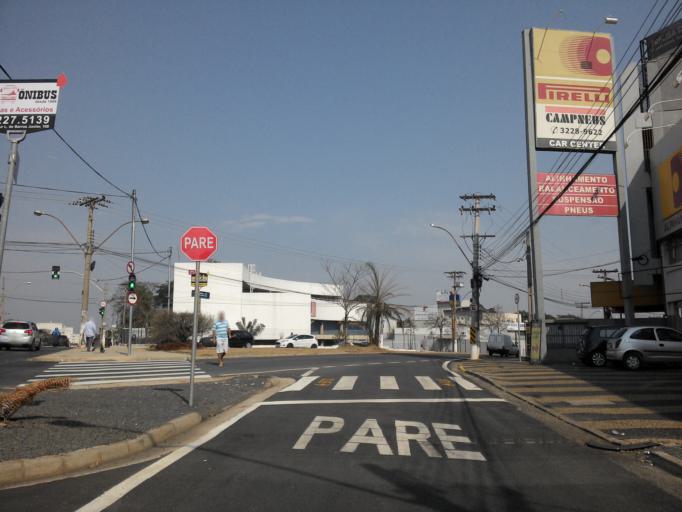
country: BR
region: Sao Paulo
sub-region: Campinas
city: Campinas
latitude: -22.9328
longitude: -47.0907
